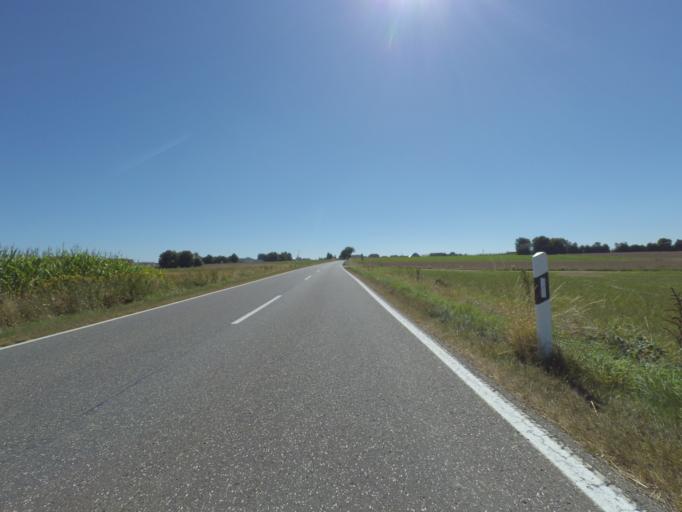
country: DE
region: Rheinland-Pfalz
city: Beuren
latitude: 50.0999
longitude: 7.0723
